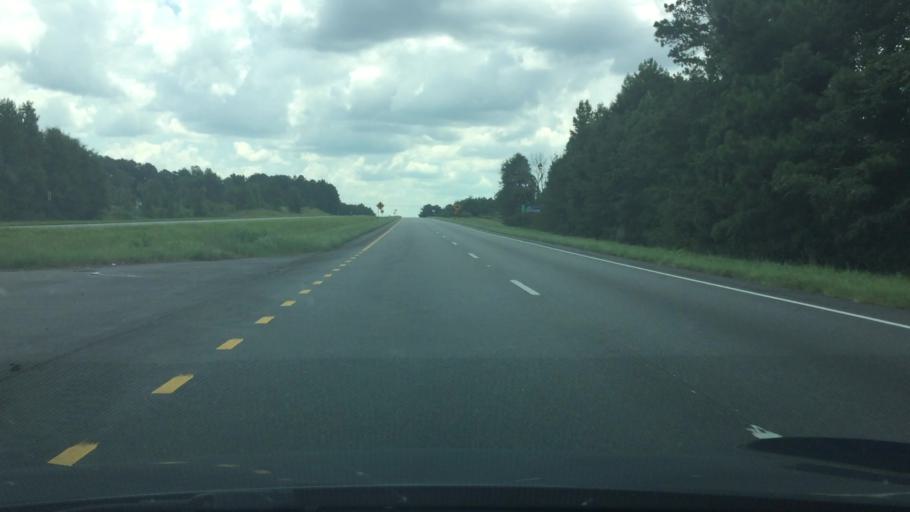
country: US
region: Alabama
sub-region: Pike County
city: Troy
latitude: 31.8877
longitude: -86.0077
